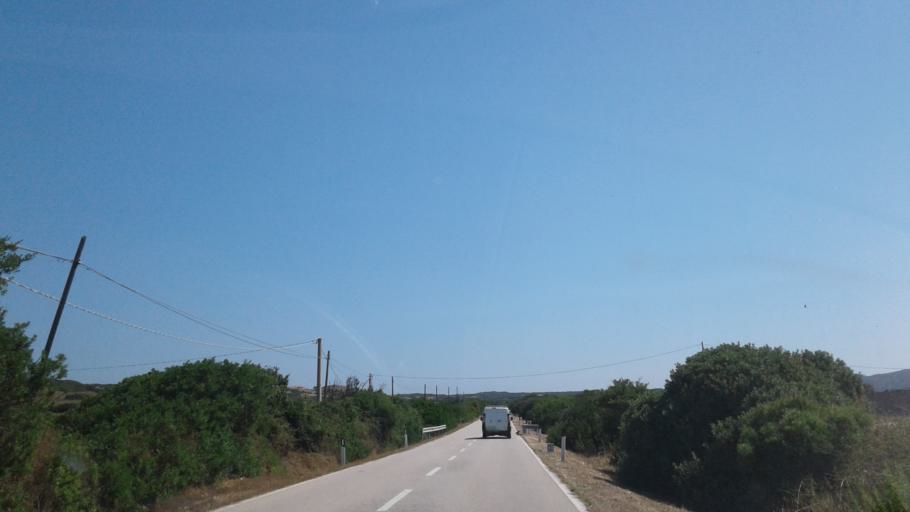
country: IT
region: Sardinia
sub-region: Provincia di Olbia-Tempio
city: Luogosanto
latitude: 41.1211
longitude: 9.2709
